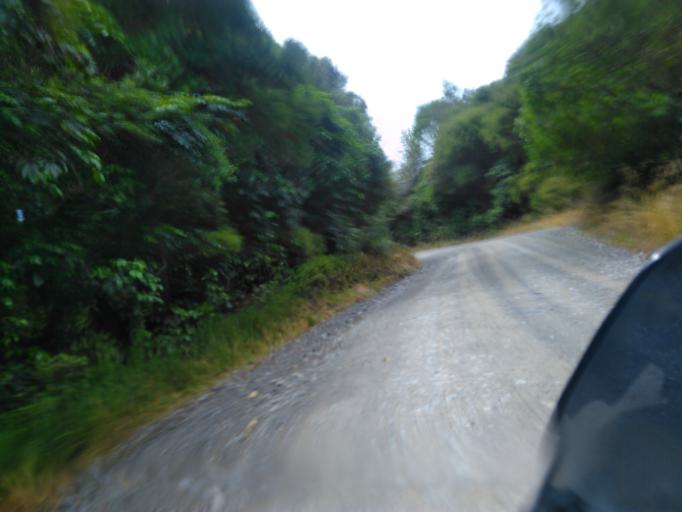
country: NZ
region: Gisborne
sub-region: Gisborne District
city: Gisborne
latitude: -38.1674
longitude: 178.1354
